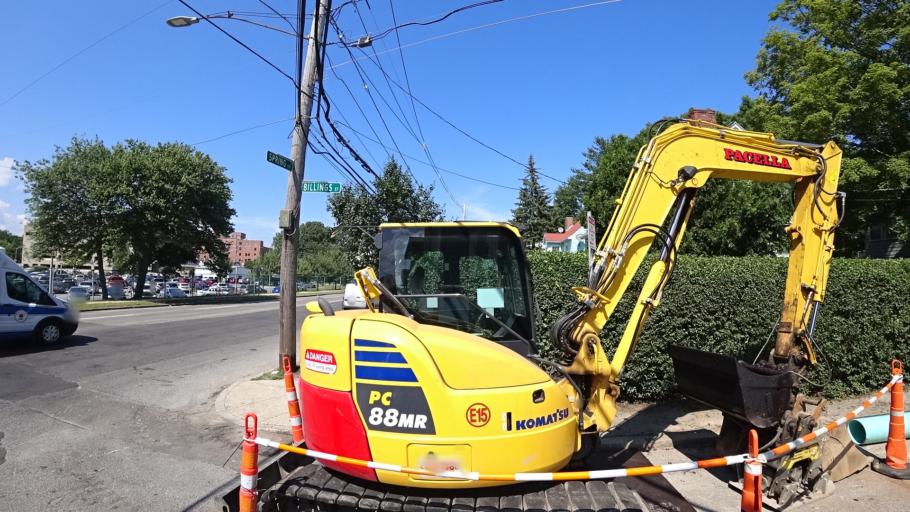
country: US
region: Massachusetts
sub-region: Norfolk County
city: Dedham
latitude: 42.2722
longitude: -71.1716
